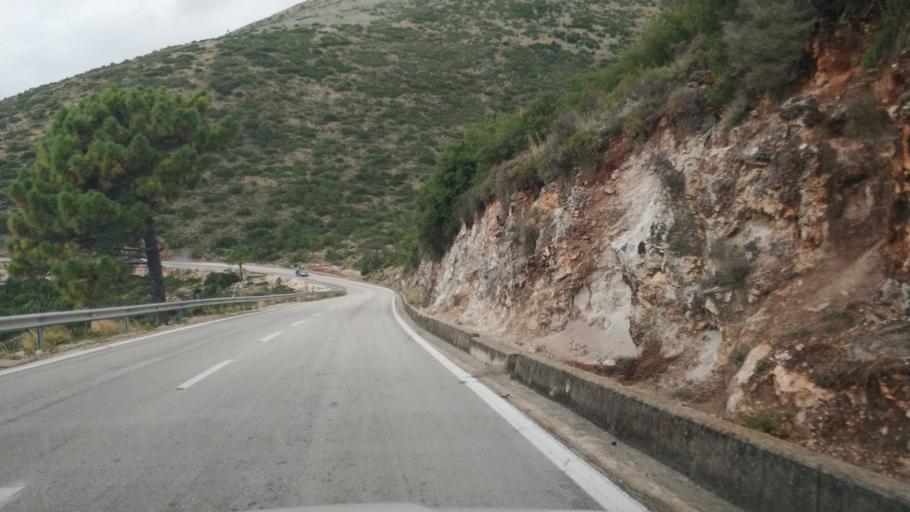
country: AL
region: Vlore
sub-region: Rrethi i Vlores
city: Vranisht
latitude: 40.1443
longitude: 19.6612
